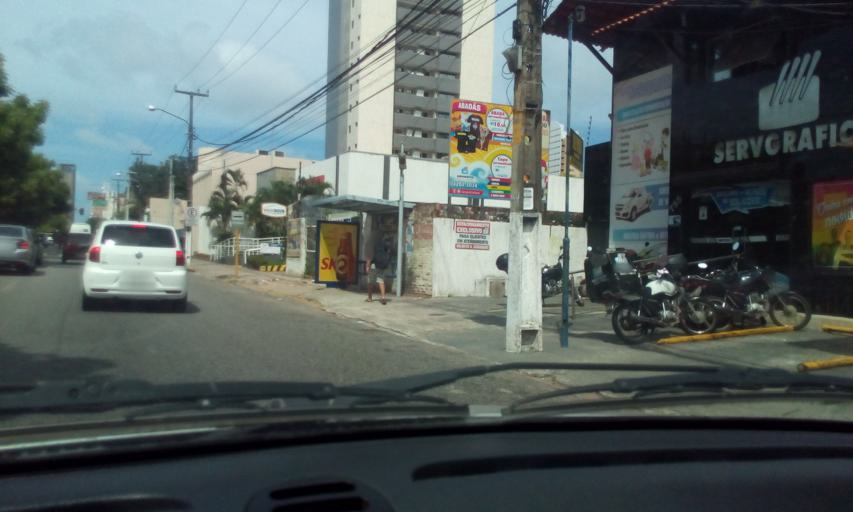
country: BR
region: Rio Grande do Norte
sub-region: Natal
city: Natal
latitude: -5.7895
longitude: -35.2050
